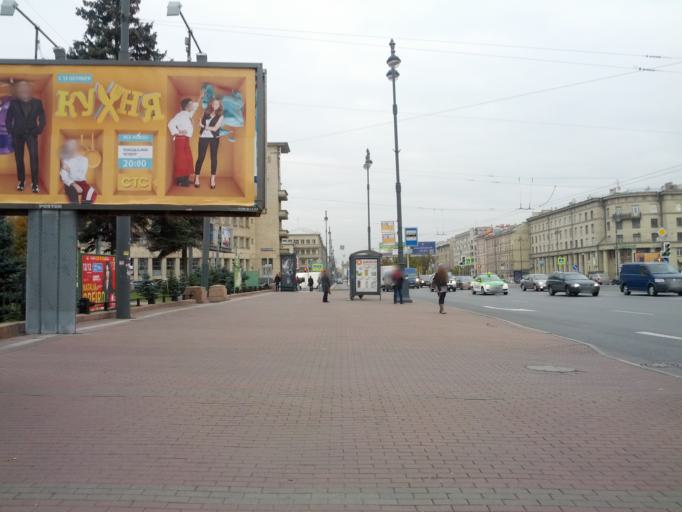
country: RU
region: St.-Petersburg
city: Admiralteisky
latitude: 59.8833
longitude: 30.3199
